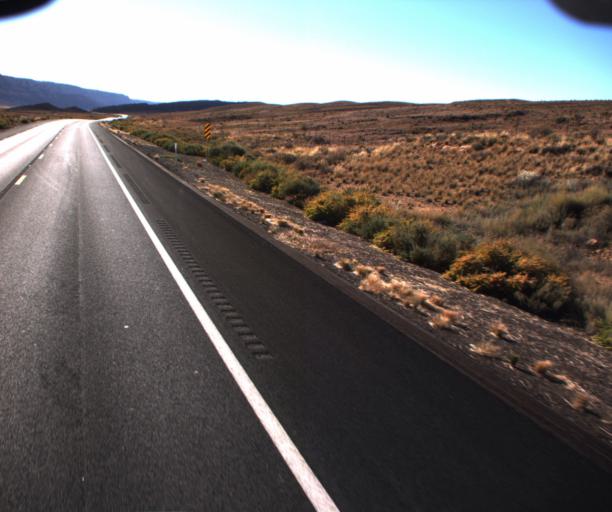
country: US
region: Arizona
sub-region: Coconino County
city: LeChee
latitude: 36.5292
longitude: -111.6054
